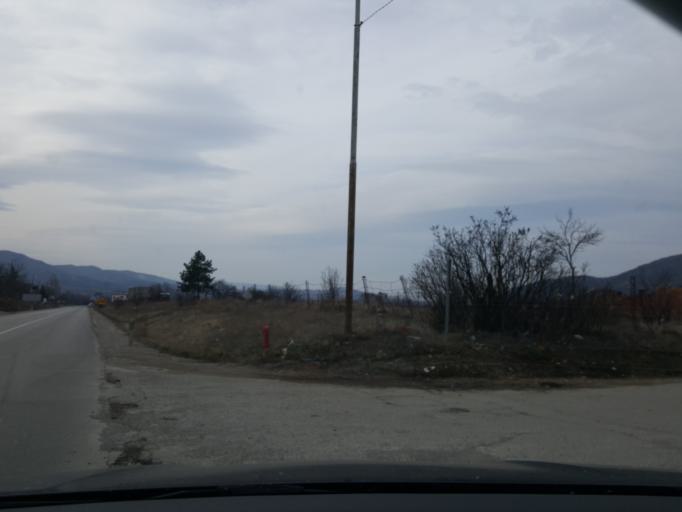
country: RS
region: Central Serbia
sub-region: Pirotski Okrug
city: Dimitrovgrad
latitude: 43.0103
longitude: 22.7526
